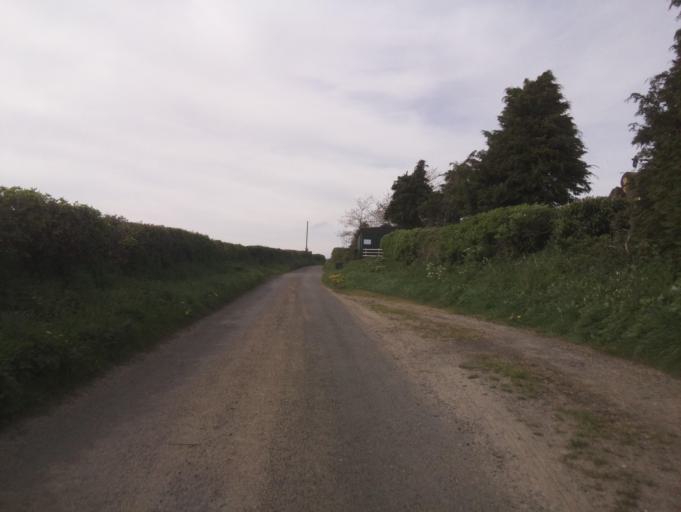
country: GB
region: England
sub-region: Dorset
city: Sherborne
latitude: 50.9693
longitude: -2.5049
